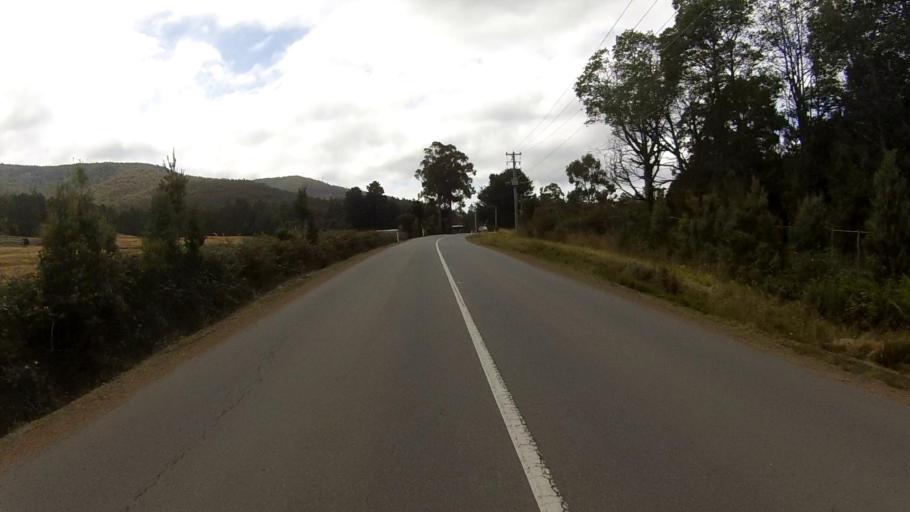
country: AU
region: Tasmania
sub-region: Kingborough
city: Kettering
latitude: -43.1196
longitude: 147.1855
